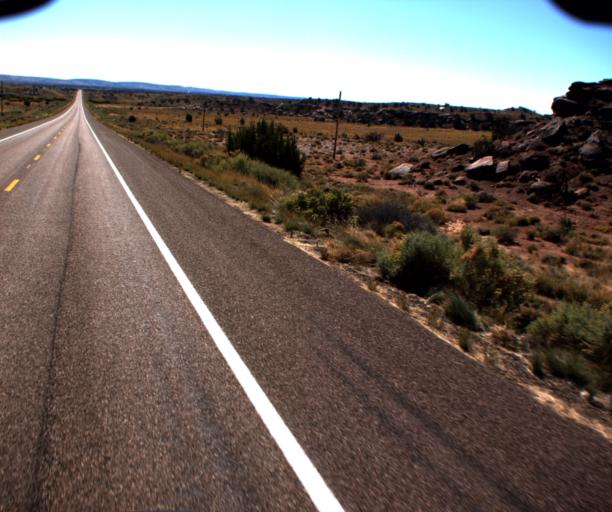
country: US
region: Arizona
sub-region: Apache County
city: Saint Johns
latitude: 34.6355
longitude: -109.6853
